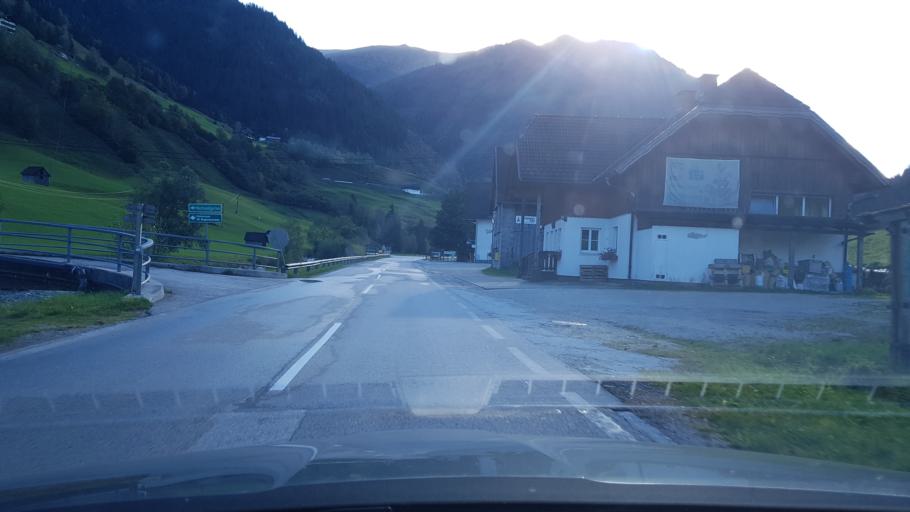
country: AT
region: Styria
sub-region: Politischer Bezirk Liezen
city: Grosssolk
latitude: 47.3767
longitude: 14.0015
